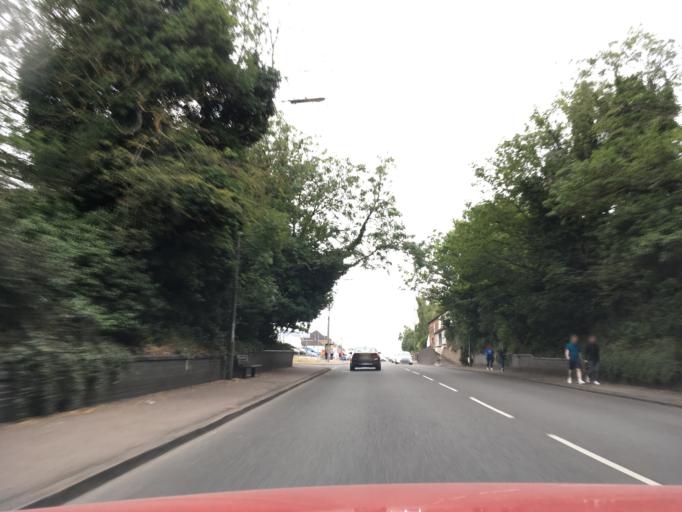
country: GB
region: England
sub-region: Central Bedfordshire
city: Dunstable
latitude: 51.8798
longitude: -0.5117
